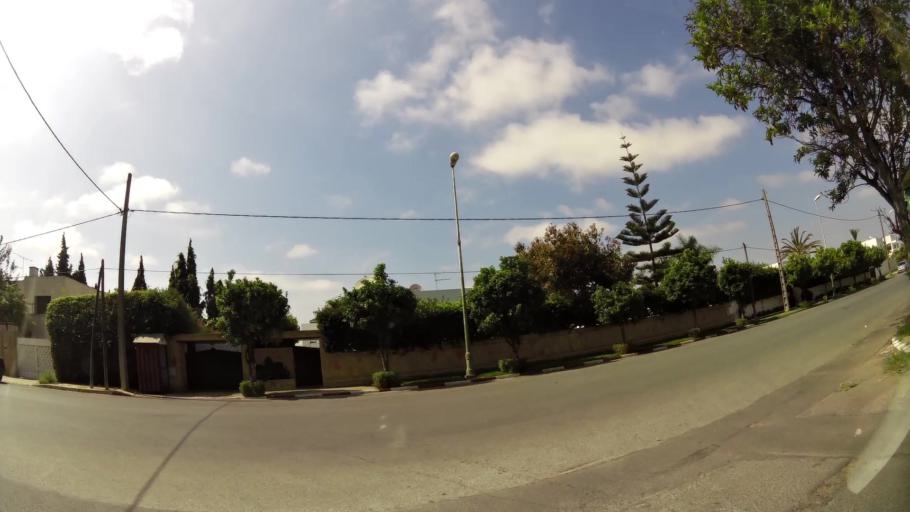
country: MA
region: Rabat-Sale-Zemmour-Zaer
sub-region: Rabat
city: Rabat
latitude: 33.9857
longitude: -6.8341
